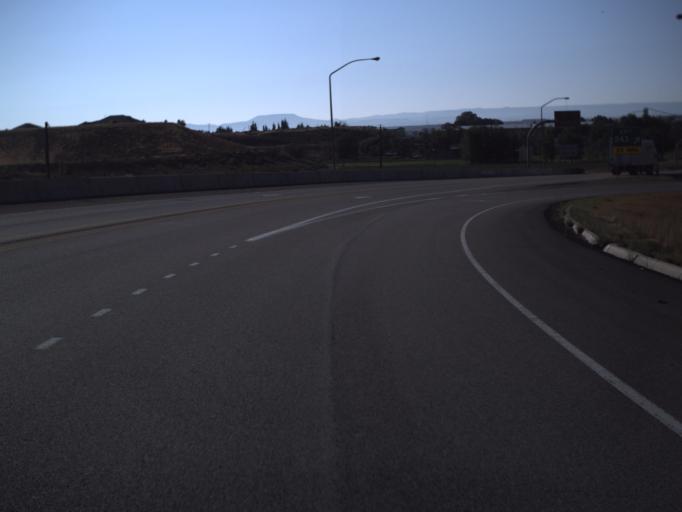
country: US
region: Utah
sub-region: Carbon County
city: Price
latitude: 39.5864
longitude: -110.7885
